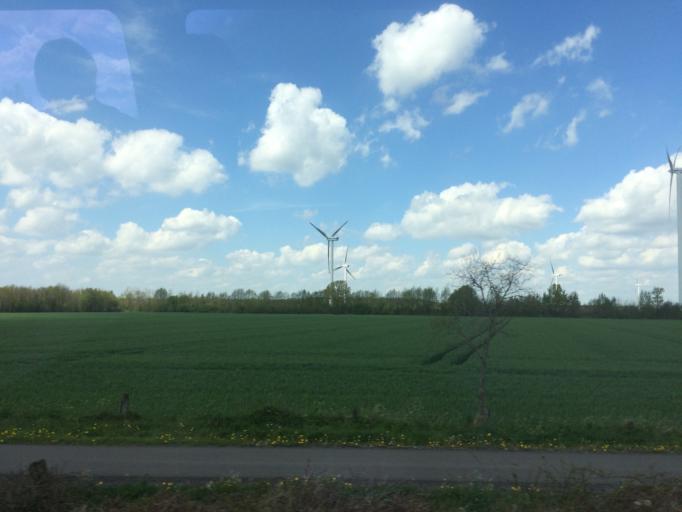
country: DE
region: Schleswig-Holstein
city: Hasenkrug
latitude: 53.9987
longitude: 9.8404
